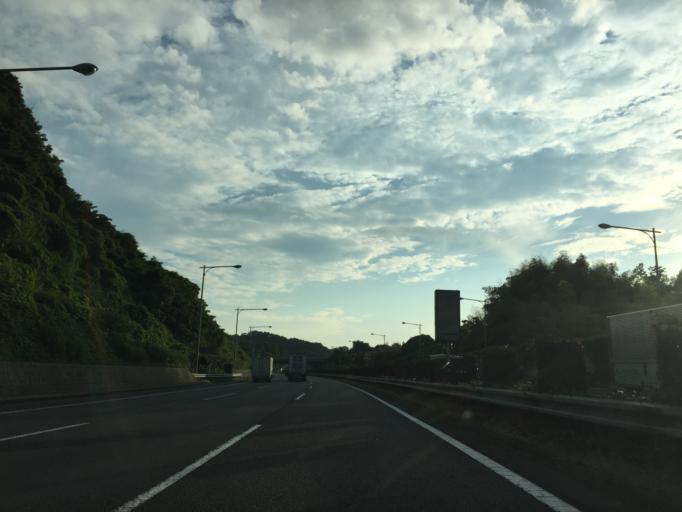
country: JP
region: Kanagawa
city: Hadano
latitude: 35.3403
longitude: 139.1884
